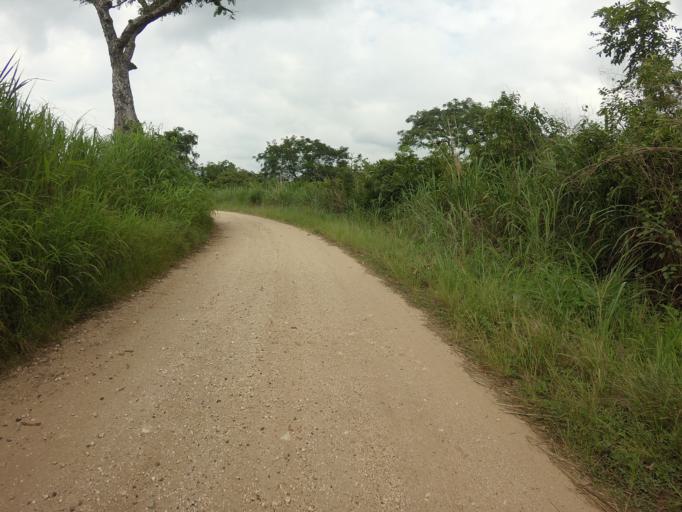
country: TG
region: Plateaux
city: Kpalime
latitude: 6.8667
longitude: 0.4429
